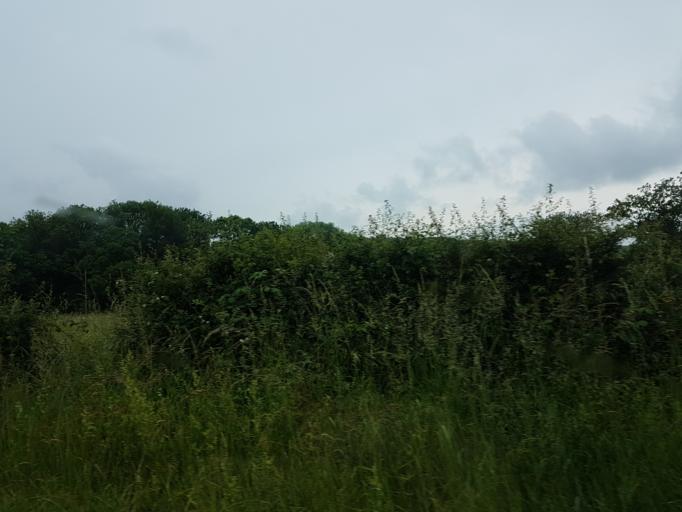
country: FR
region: Bourgogne
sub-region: Departement de la Nievre
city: Corbigny
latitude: 47.1924
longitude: 3.7341
